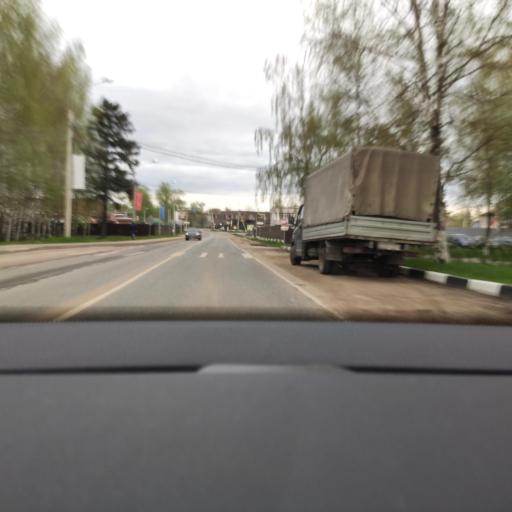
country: RU
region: Moskovskaya
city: Novopodrezkovo
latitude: 55.9954
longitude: 37.3417
